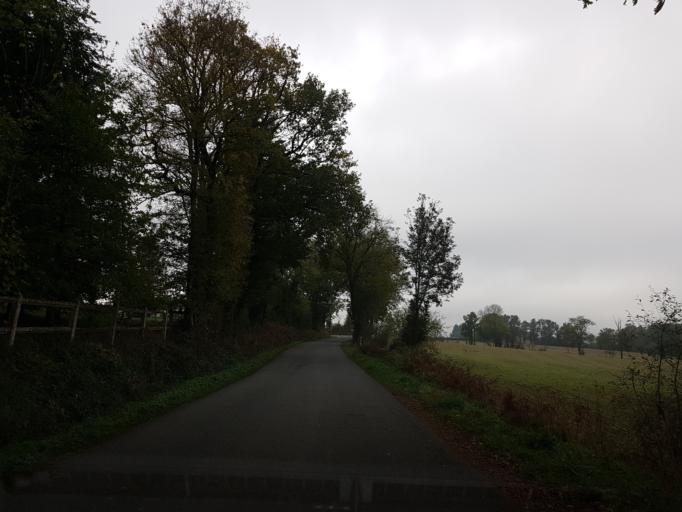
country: FR
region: Poitou-Charentes
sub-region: Departement de la Charente
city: Chabanais
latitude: 45.8844
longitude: 0.7201
